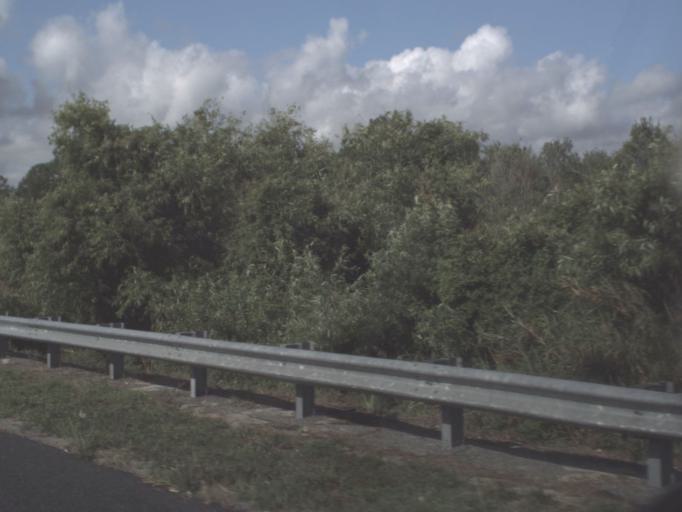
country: US
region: Florida
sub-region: Lake County
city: Leesburg
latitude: 28.7868
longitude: -81.8878
